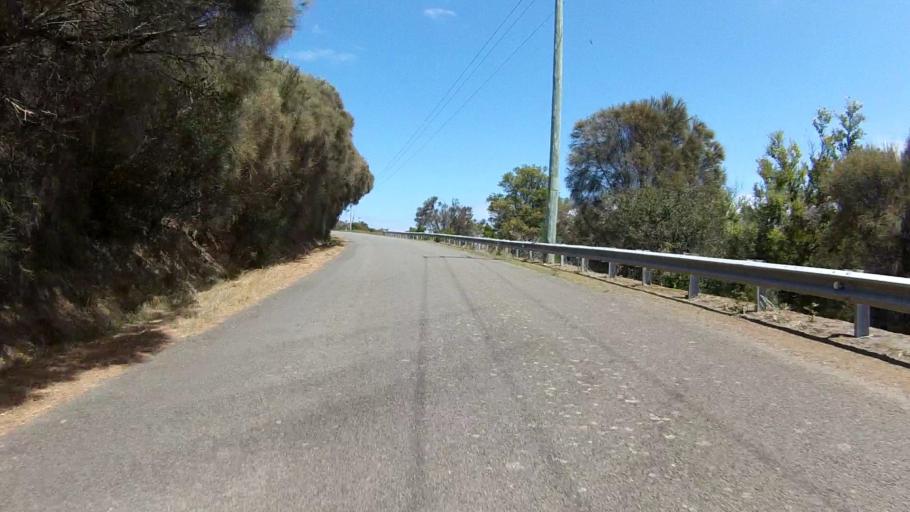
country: AU
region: Tasmania
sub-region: Clarence
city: Lauderdale
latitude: -42.9199
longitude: 147.4732
